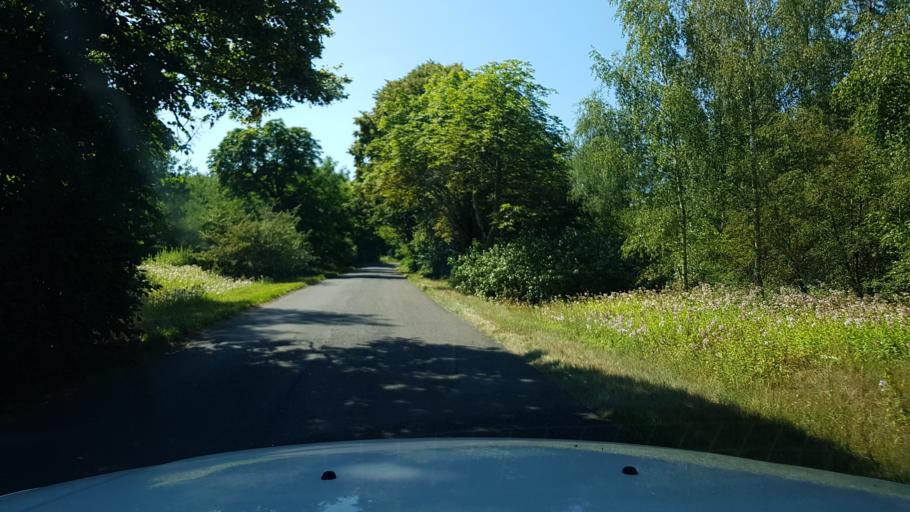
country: PL
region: West Pomeranian Voivodeship
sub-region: Powiat goleniowski
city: Goleniow
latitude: 53.4659
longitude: 14.7147
